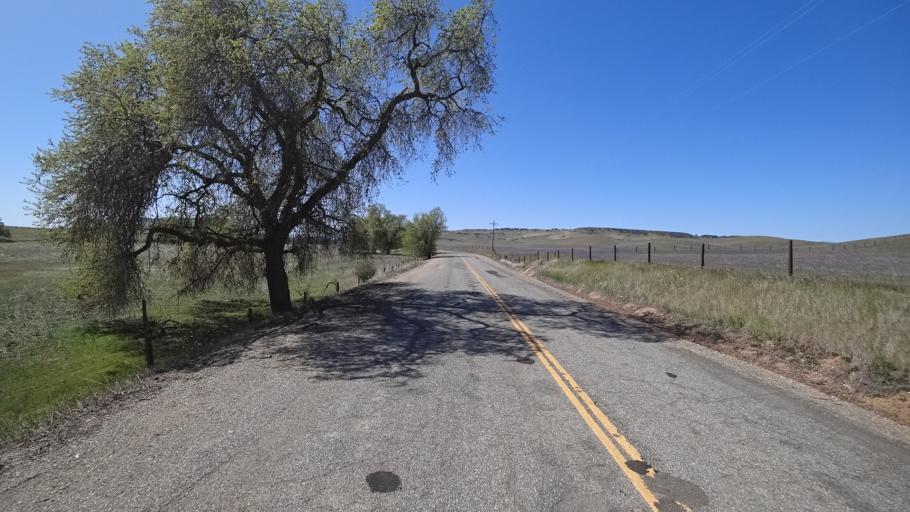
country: US
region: California
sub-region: Glenn County
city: Orland
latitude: 39.7780
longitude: -122.3127
